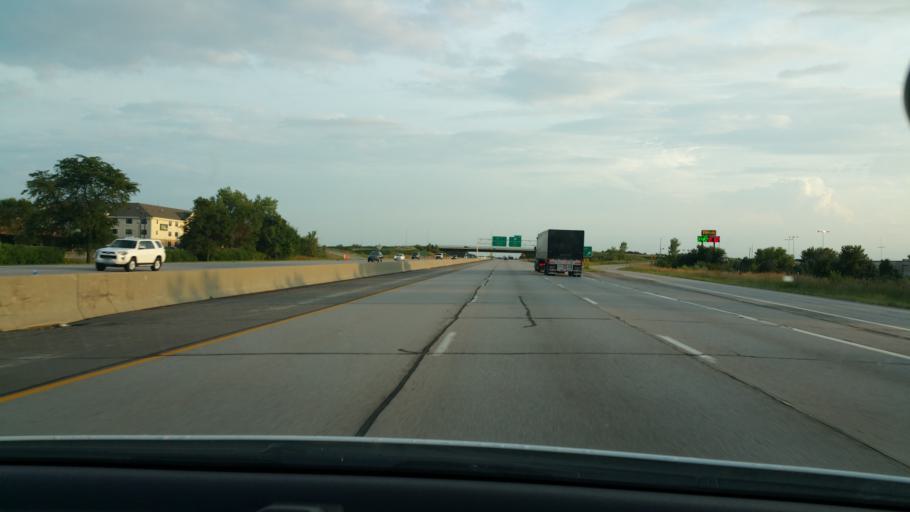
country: US
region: Iowa
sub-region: Polk County
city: Grimes
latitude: 41.6348
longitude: -93.7770
